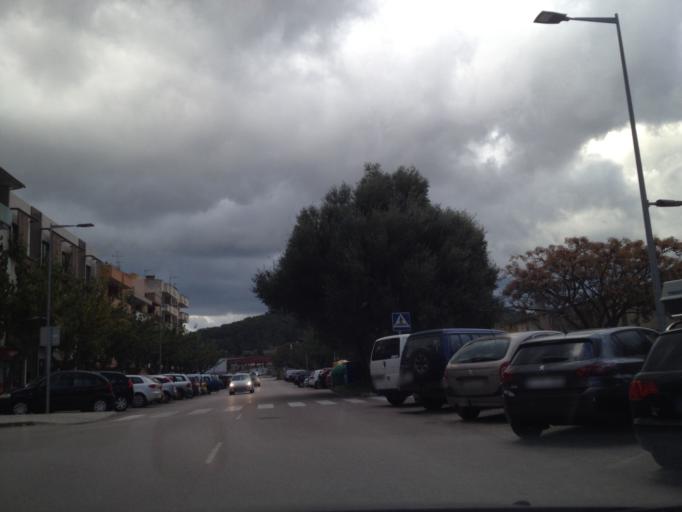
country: ES
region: Balearic Islands
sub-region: Illes Balears
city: Pollenca
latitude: 39.8762
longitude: 3.0203
